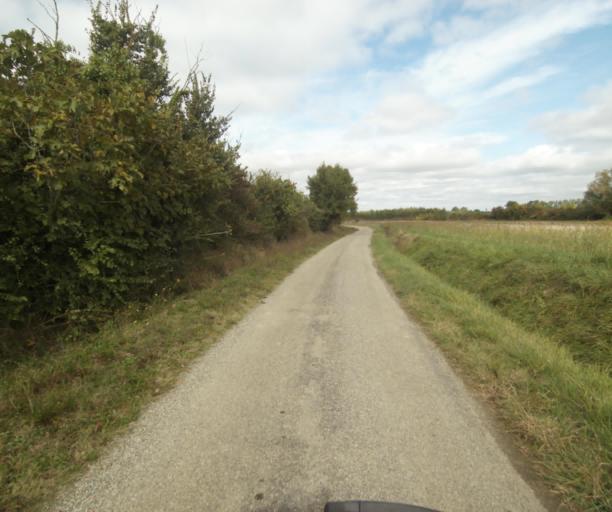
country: FR
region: Midi-Pyrenees
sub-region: Departement du Tarn-et-Garonne
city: Finhan
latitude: 43.9219
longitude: 1.2080
